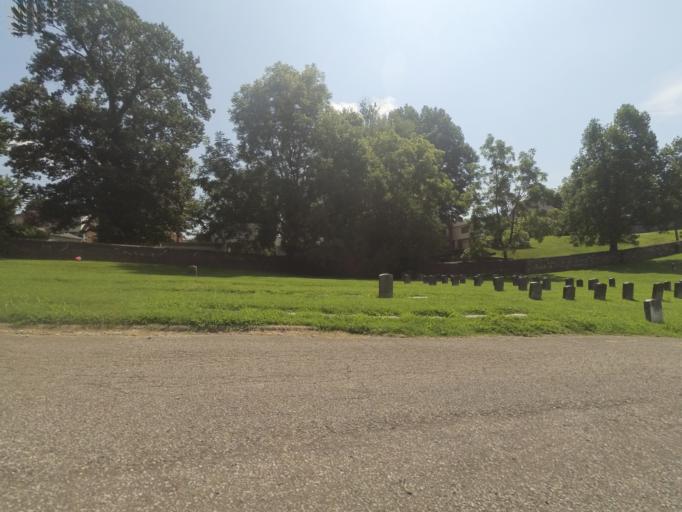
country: US
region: West Virginia
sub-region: Cabell County
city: Huntington
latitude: 38.4084
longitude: -82.4125
